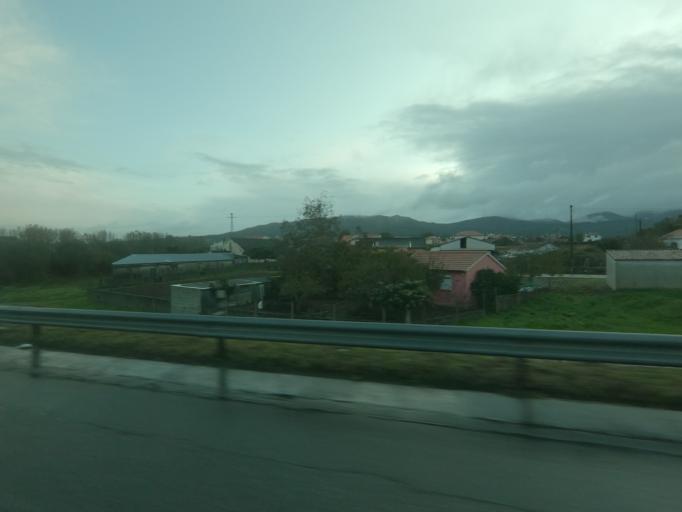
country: PT
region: Viana do Castelo
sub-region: Valenca
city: Valenza
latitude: 42.0083
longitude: -8.6471
